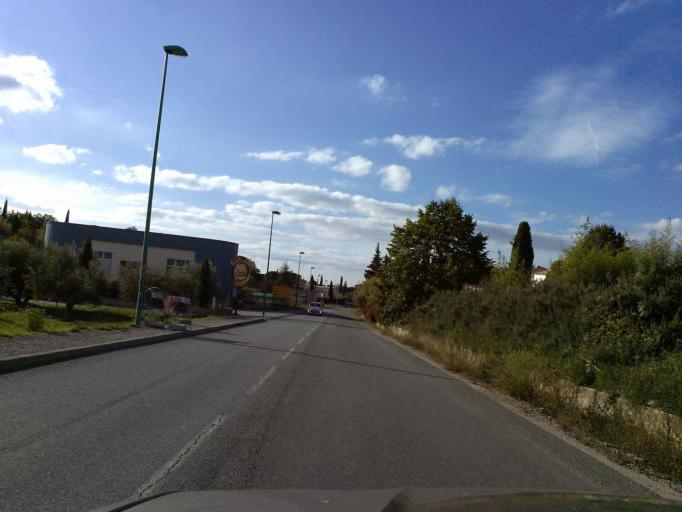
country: FR
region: Provence-Alpes-Cote d'Azur
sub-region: Departement des Alpes-de-Haute-Provence
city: Valensole
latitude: 43.8356
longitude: 5.9767
